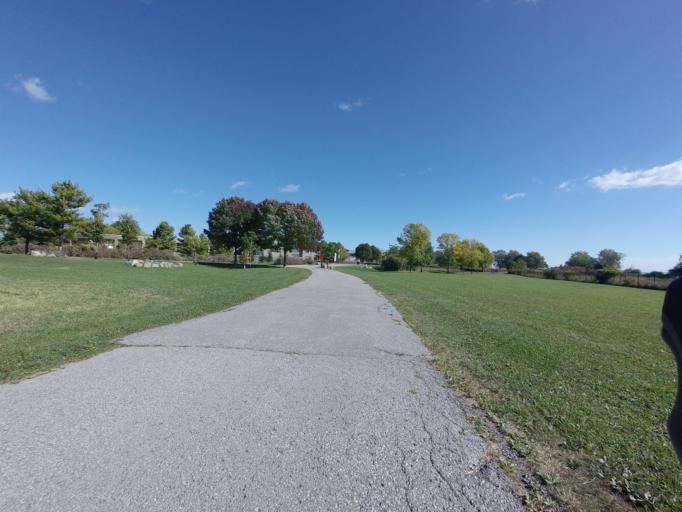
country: CA
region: Ontario
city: Ajax
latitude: 43.8480
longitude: -78.9491
